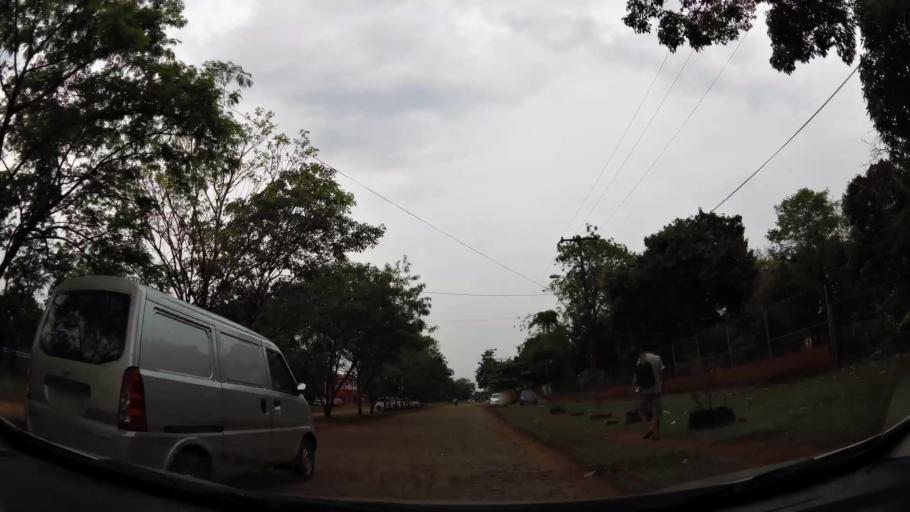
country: PY
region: Alto Parana
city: Presidente Franco
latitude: -25.5396
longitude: -54.6511
